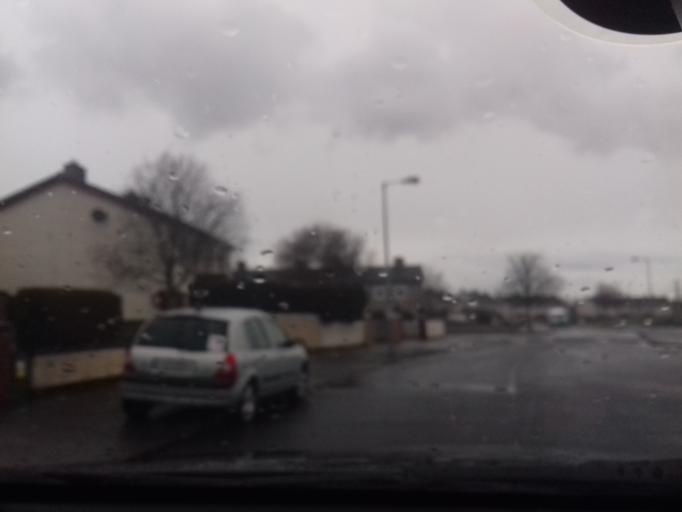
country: IE
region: Leinster
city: Hartstown
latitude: 53.3921
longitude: -6.4065
